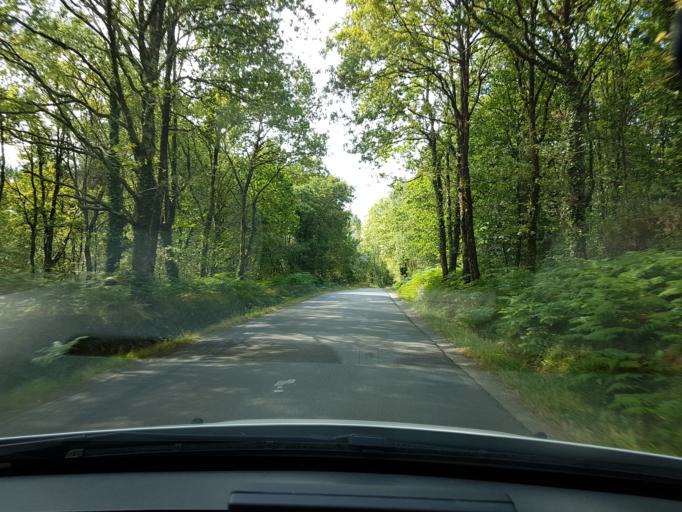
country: FR
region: Brittany
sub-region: Departement du Morbihan
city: Sainte-Helene
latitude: 47.7107
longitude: -3.2126
